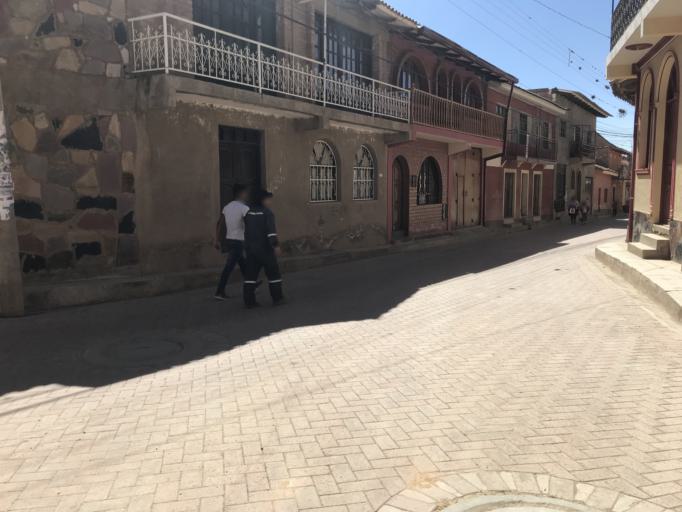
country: BO
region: Cochabamba
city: Tarata
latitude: -17.6149
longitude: -66.0271
